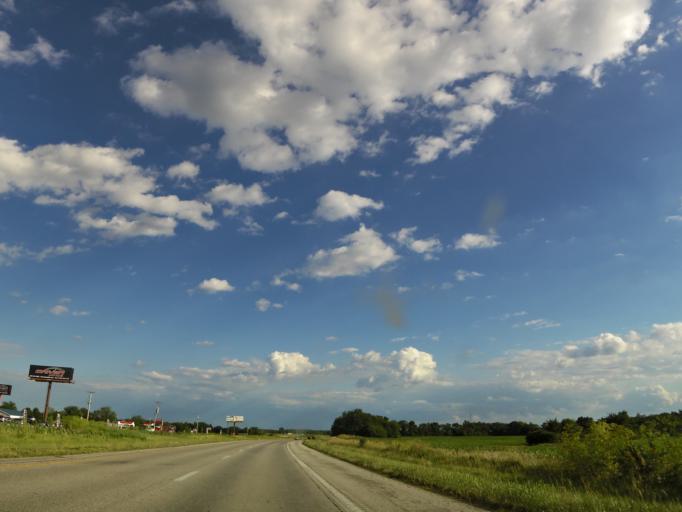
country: US
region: Missouri
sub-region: Lincoln County
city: Troy
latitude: 39.1381
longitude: -90.9652
